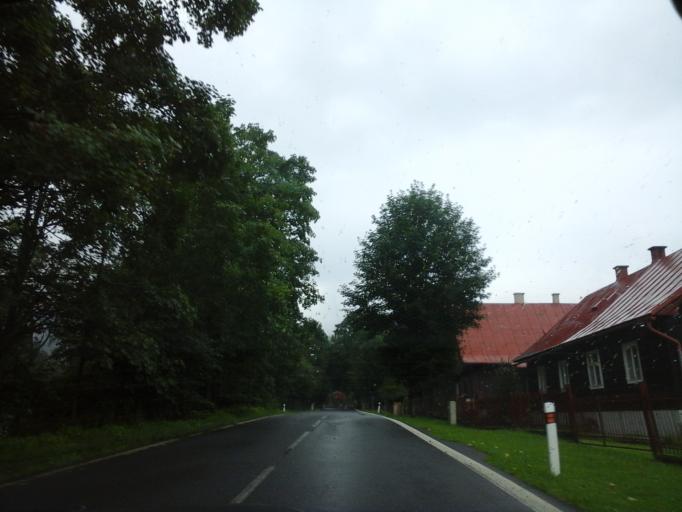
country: PL
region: Lesser Poland Voivodeship
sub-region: Powiat tatrzanski
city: Bukowina Tatrzanska
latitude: 49.2689
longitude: 20.1459
